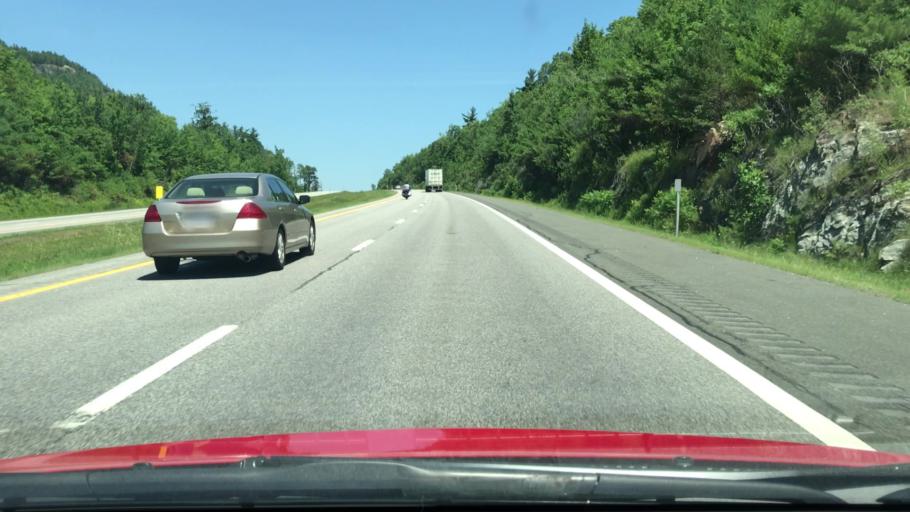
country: US
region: New York
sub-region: Essex County
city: Keeseville
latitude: 44.3926
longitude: -73.5027
